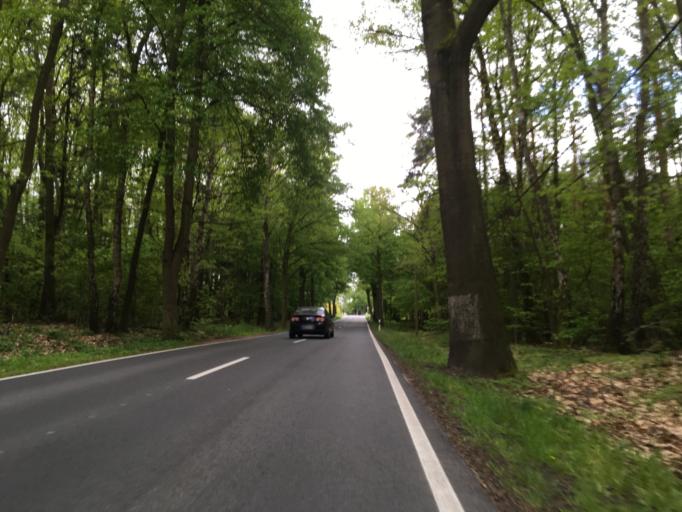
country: DE
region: Brandenburg
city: Bernau bei Berlin
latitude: 52.6270
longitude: 13.6117
